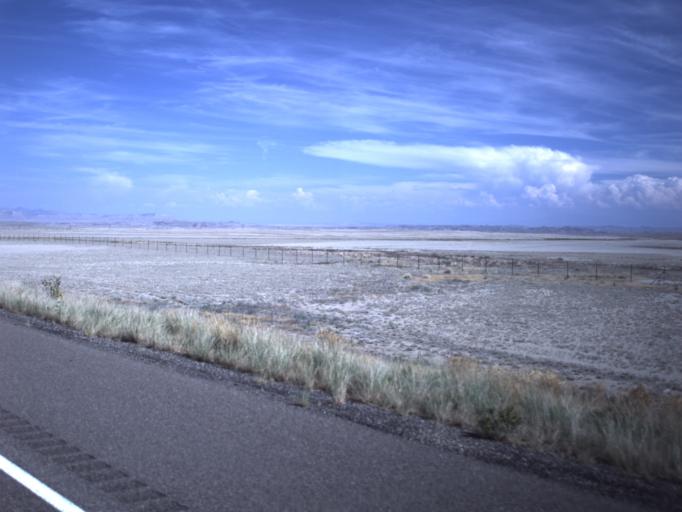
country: US
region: Utah
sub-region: Carbon County
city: East Carbon City
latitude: 38.9528
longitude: -110.3101
